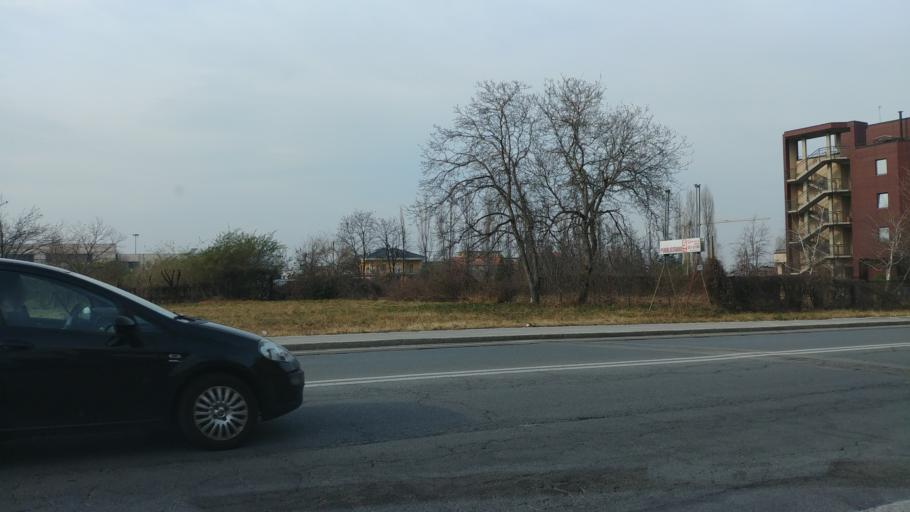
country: IT
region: Piedmont
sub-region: Provincia di Cuneo
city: Cuneo
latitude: 44.3762
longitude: 7.5261
